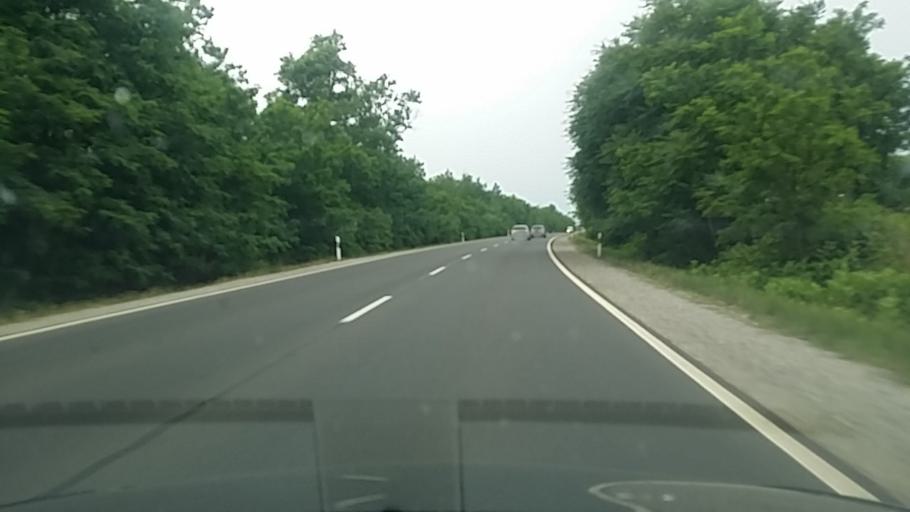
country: HU
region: Hajdu-Bihar
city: Teglas
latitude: 47.7370
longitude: 21.6808
